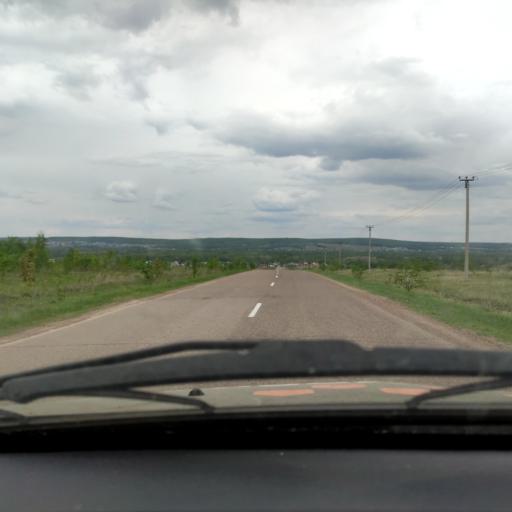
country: RU
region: Bashkortostan
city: Avdon
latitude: 54.5854
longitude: 55.7190
